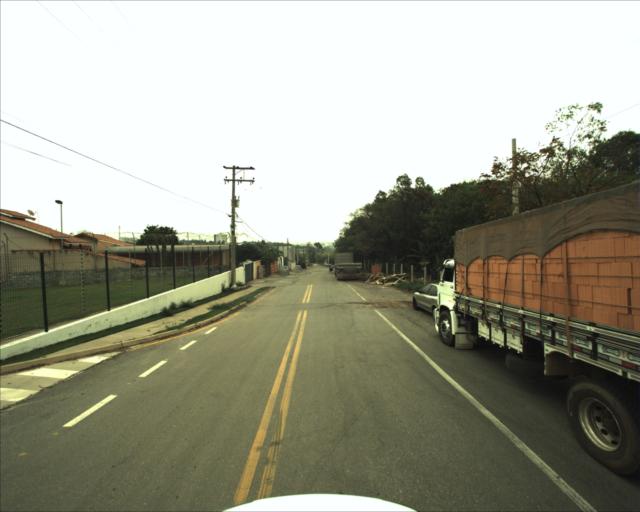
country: BR
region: Sao Paulo
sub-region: Sorocaba
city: Sorocaba
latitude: -23.4663
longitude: -47.4175
